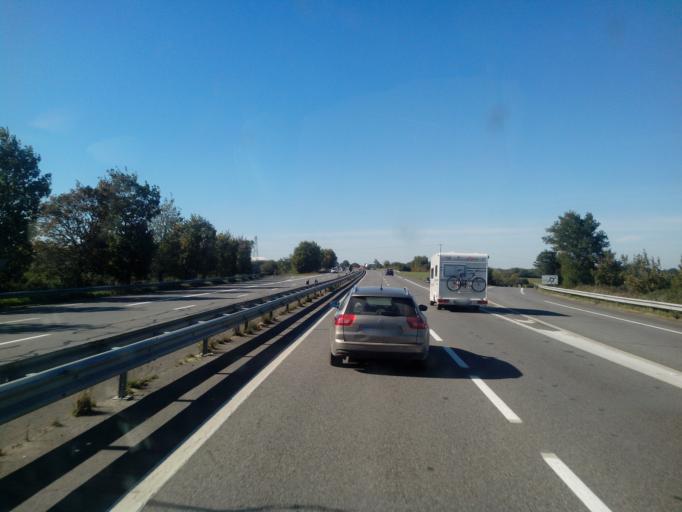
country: FR
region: Pays de la Loire
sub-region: Departement de la Loire-Atlantique
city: La Chapelle-Launay
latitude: 47.3804
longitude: -1.9625
